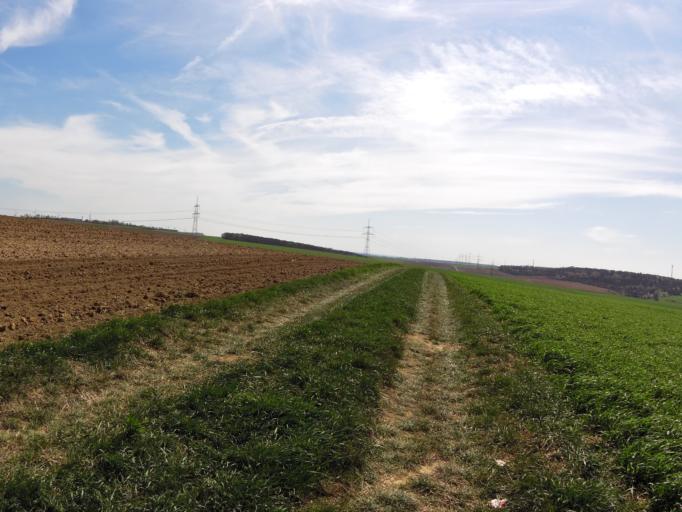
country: DE
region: Bavaria
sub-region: Regierungsbezirk Unterfranken
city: Rottendorf
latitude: 49.7931
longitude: 10.0468
